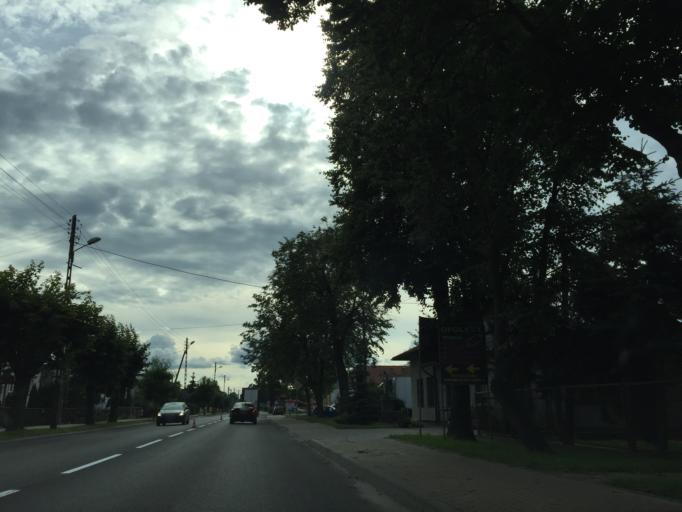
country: PL
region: Lublin Voivodeship
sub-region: Powiat lukowski
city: Lukow
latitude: 51.9259
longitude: 22.3714
